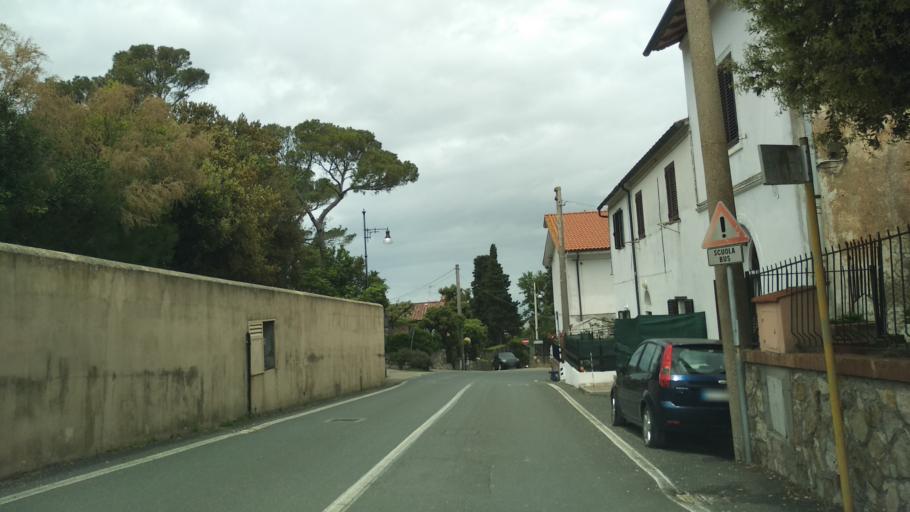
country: IT
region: Tuscany
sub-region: Provincia di Livorno
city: Quercianella
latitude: 43.4905
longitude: 10.3586
